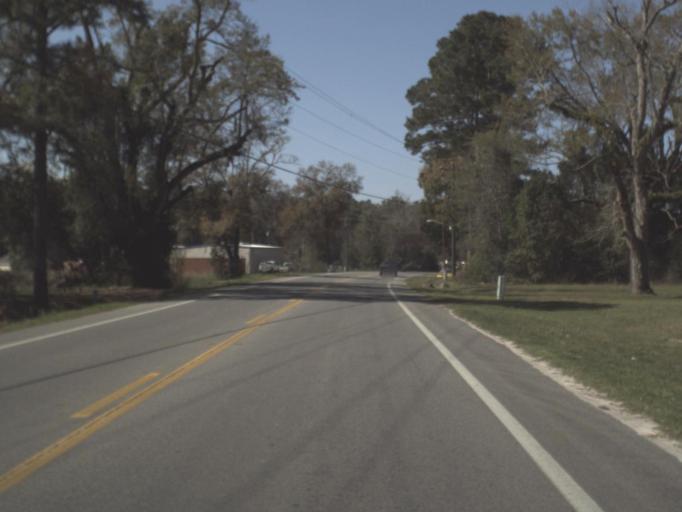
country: US
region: Florida
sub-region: Gulf County
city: Wewahitchka
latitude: 30.0990
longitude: -85.1997
